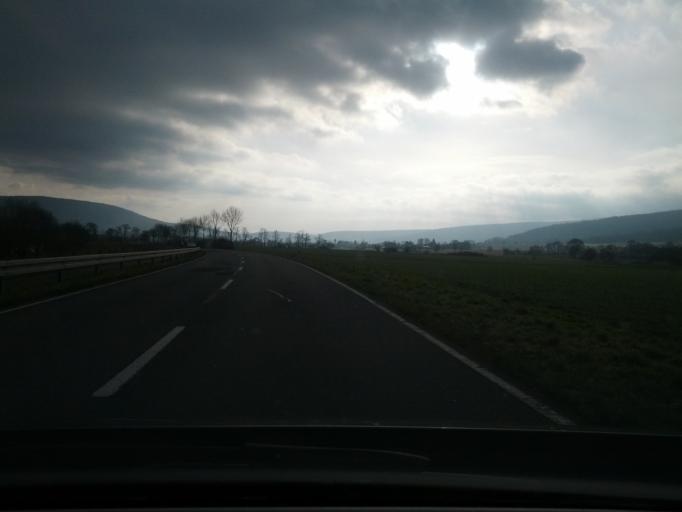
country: DE
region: Lower Saxony
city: Buhren
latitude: 51.5155
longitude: 9.5849
